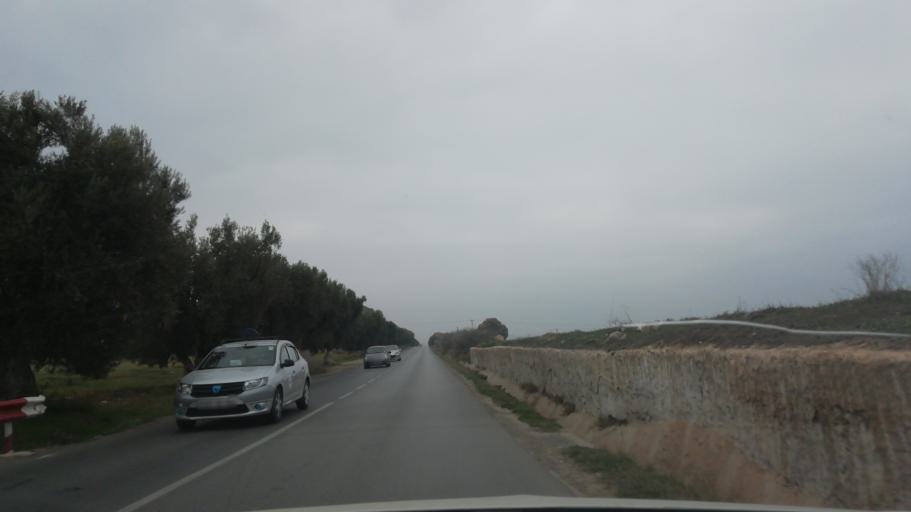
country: DZ
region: Sidi Bel Abbes
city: Sfizef
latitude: 35.2295
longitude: -0.2616
